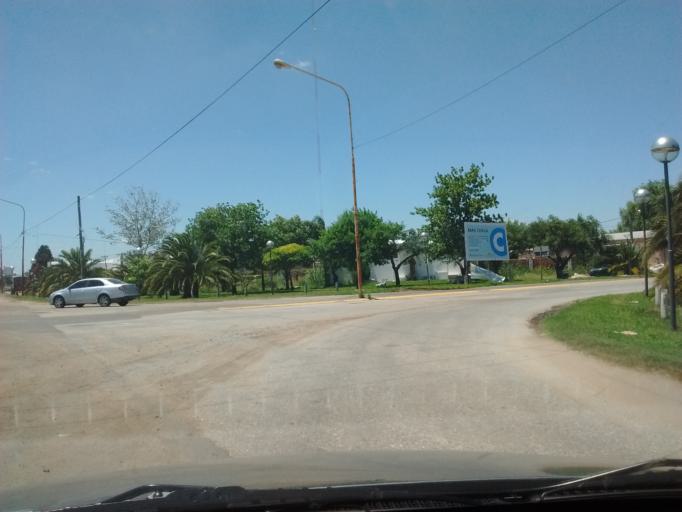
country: AR
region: Entre Rios
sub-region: Departamento de Gualeguay
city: Gualeguay
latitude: -33.1266
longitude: -59.3222
